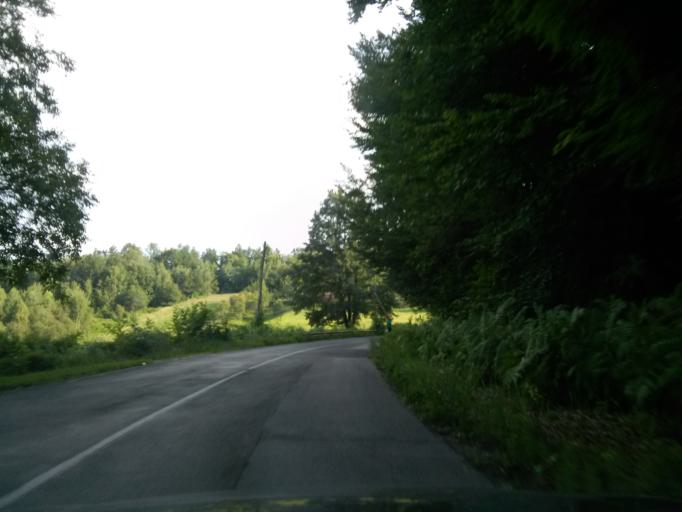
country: HR
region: Sisacko-Moslavacka
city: Gvozd
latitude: 45.3964
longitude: 15.9195
